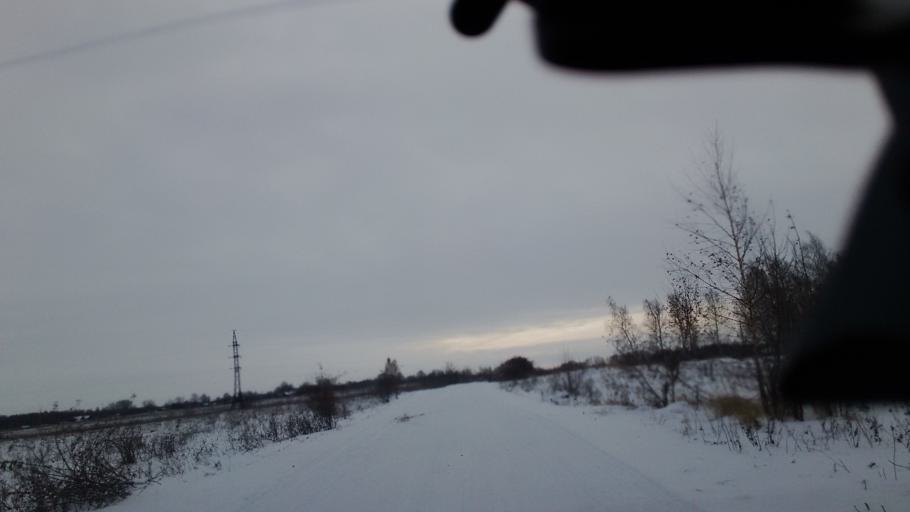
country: RU
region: Tula
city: Bogoroditsk
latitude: 53.7495
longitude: 38.1066
